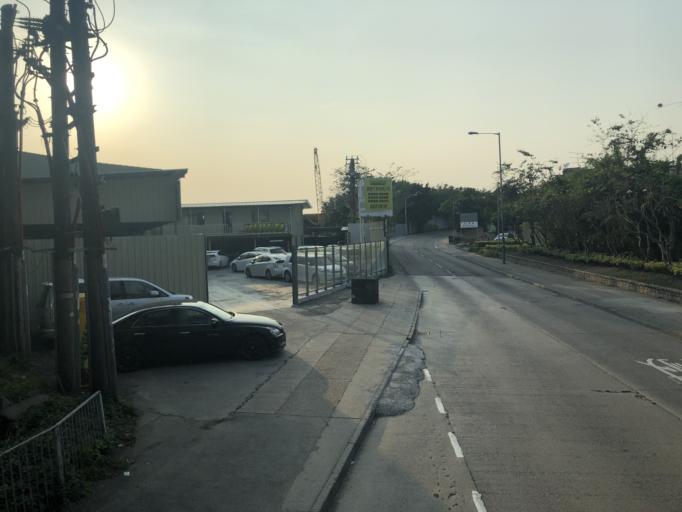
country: HK
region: Yuen Long
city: Yuen Long Kau Hui
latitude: 22.4615
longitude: 113.9889
